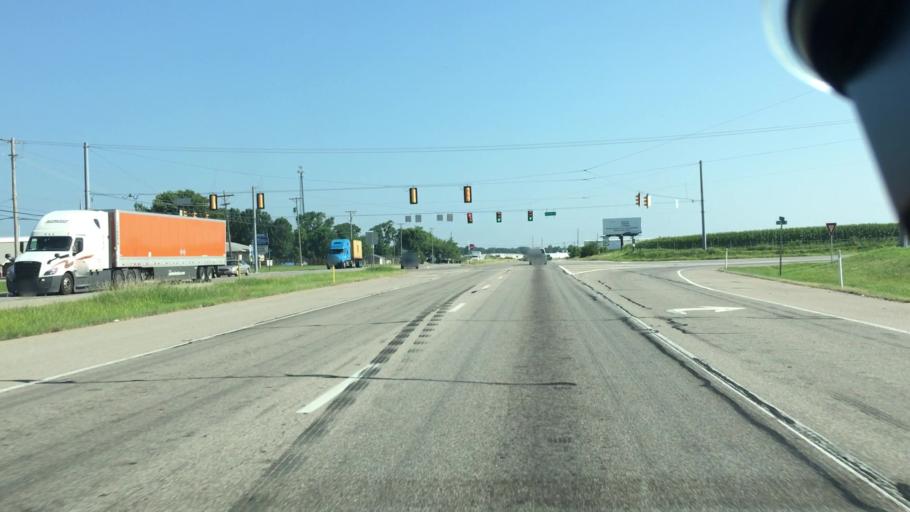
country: US
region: Indiana
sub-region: Gibson County
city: Princeton
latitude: 38.3037
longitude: -87.5673
